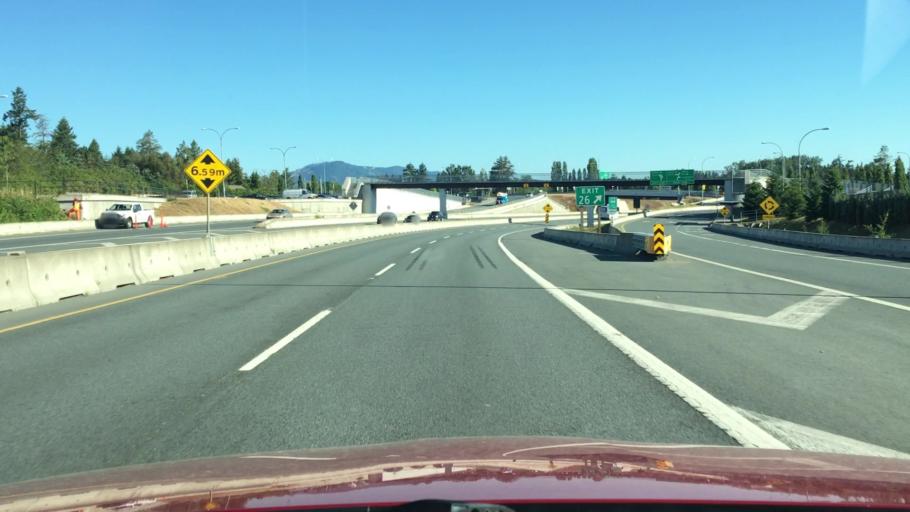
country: CA
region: British Columbia
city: North Saanich
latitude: 48.6279
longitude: -123.4116
